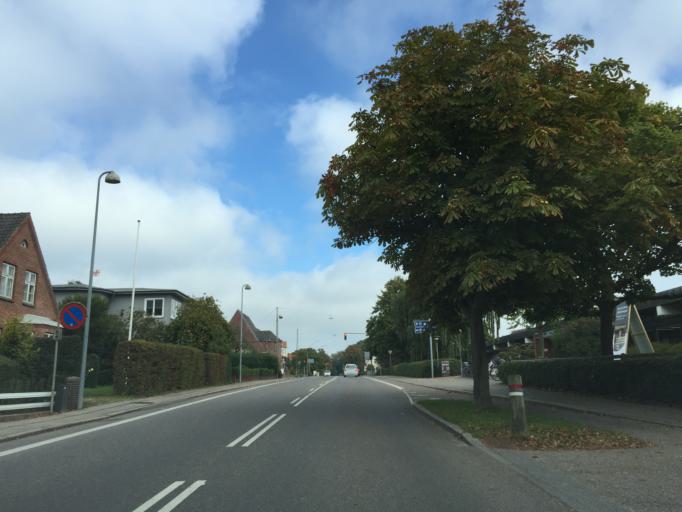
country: DK
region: South Denmark
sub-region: Sonderborg Kommune
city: Sonderborg
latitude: 54.9099
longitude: 9.7953
